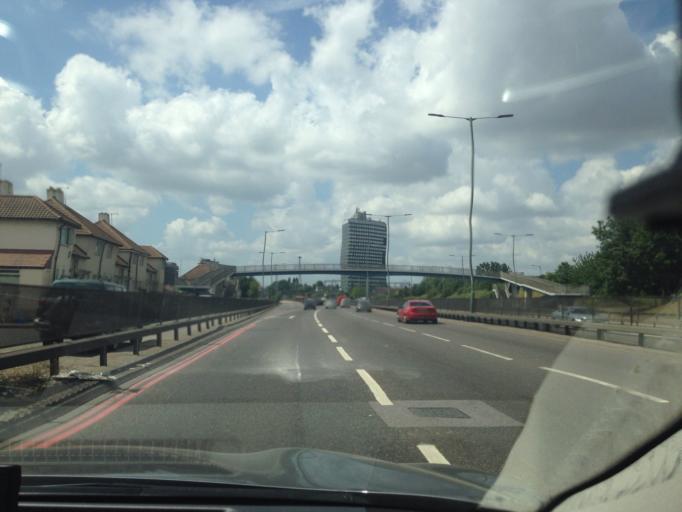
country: GB
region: England
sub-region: Greater London
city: Wembley
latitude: 51.5470
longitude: -0.2668
